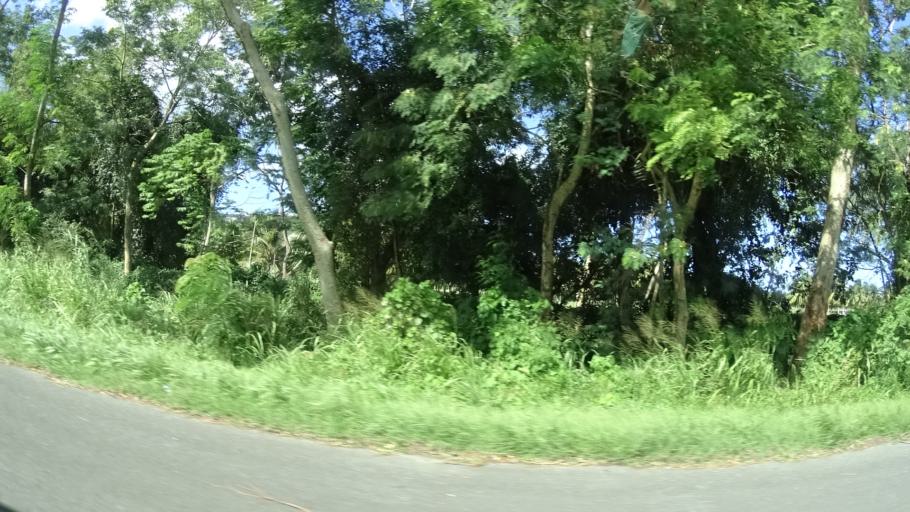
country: PR
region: Luquillo
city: Playa Fortuna
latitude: 18.3748
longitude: -65.7588
